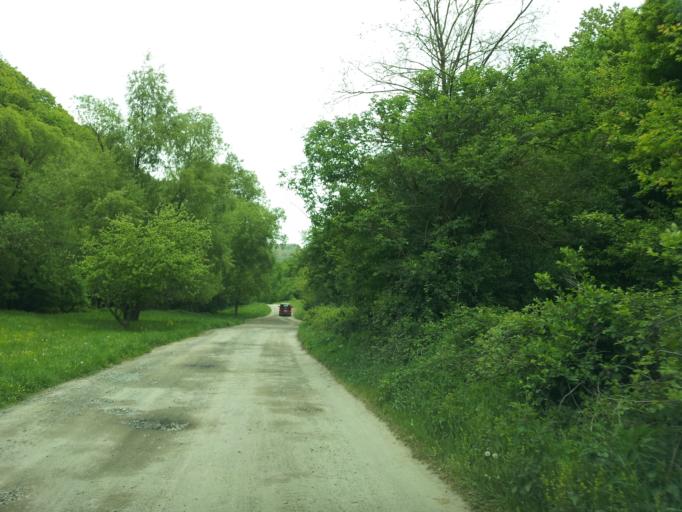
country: HU
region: Baranya
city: Hosszuheteny
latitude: 46.1806
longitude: 18.3515
